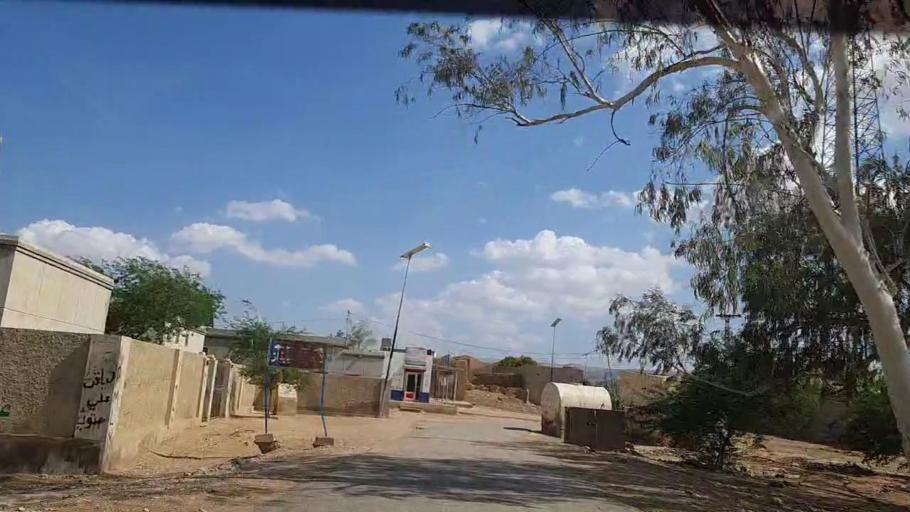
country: PK
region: Sindh
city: Johi
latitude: 26.4974
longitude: 67.4317
